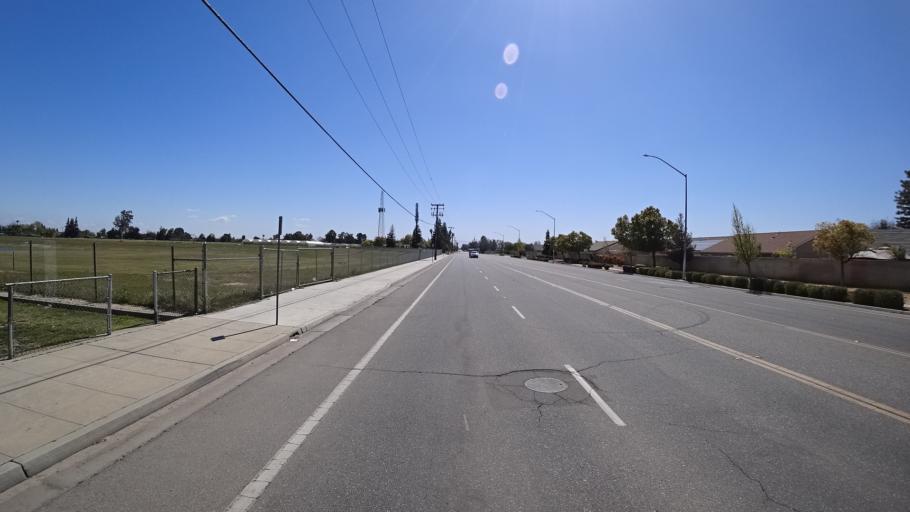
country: US
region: California
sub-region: Fresno County
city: West Park
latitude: 36.7699
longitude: -119.8623
